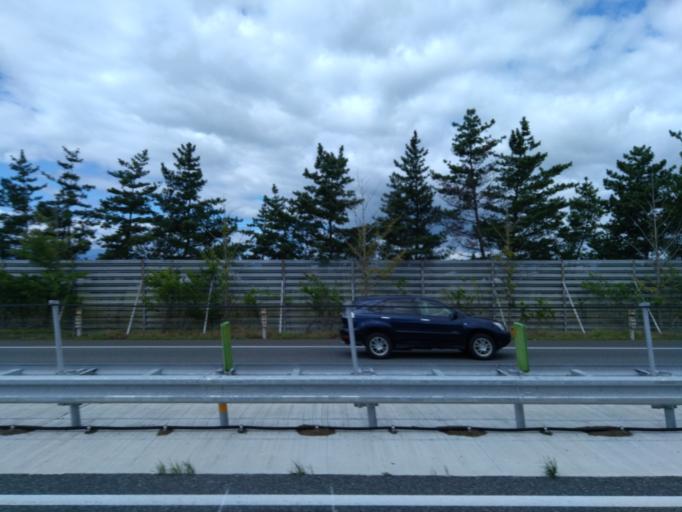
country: JP
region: Miyagi
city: Furukawa
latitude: 38.5399
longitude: 140.9304
